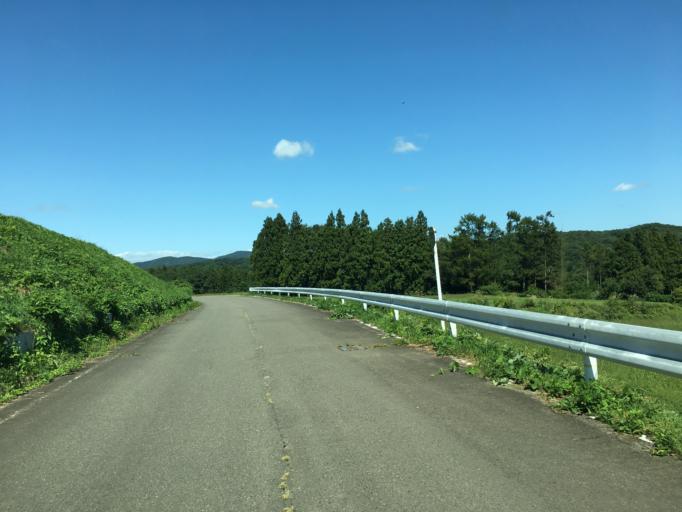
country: JP
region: Fukushima
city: Ishikawa
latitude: 37.2619
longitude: 140.5512
